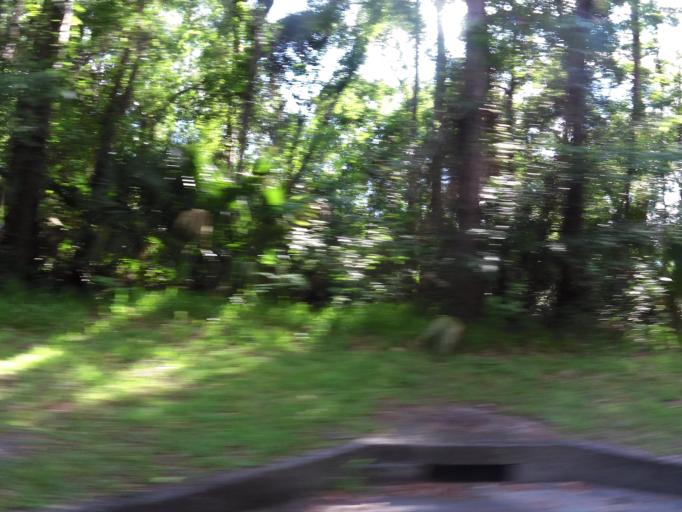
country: US
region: Florida
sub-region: Clay County
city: Green Cove Springs
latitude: 29.9907
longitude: -81.6947
